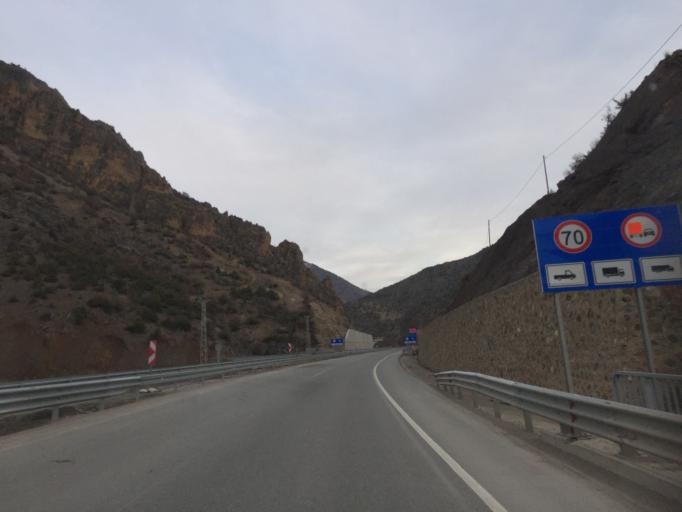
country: TR
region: Gumushane
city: Gumushkhane
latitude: 40.5236
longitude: 39.3991
